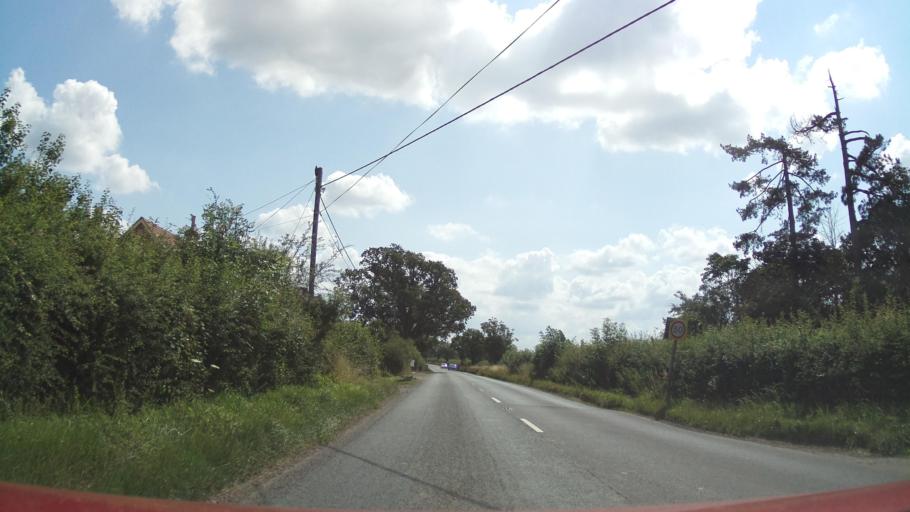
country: GB
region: England
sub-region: Wiltshire
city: Charlton
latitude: 51.5671
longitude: -2.0640
